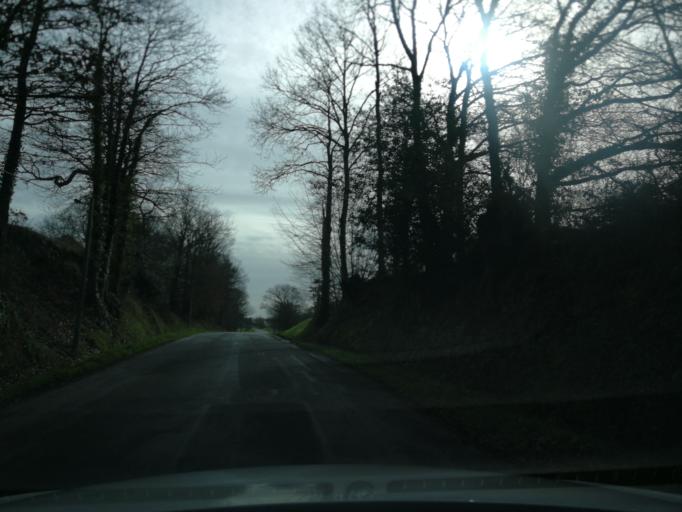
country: FR
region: Brittany
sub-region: Departement d'Ille-et-Vilaine
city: Bourg-des-Comptes
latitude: 47.9173
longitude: -1.7121
